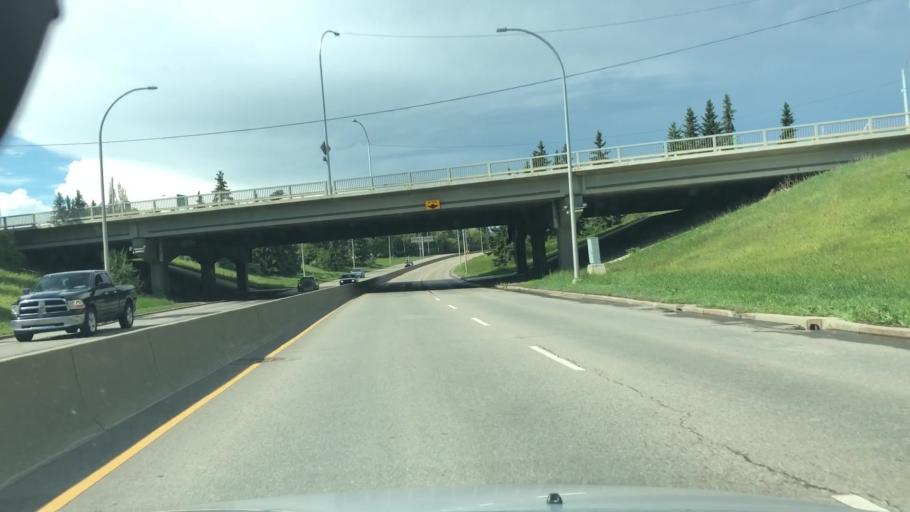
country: CA
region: Alberta
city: Edmonton
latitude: 53.5504
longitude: -113.5494
